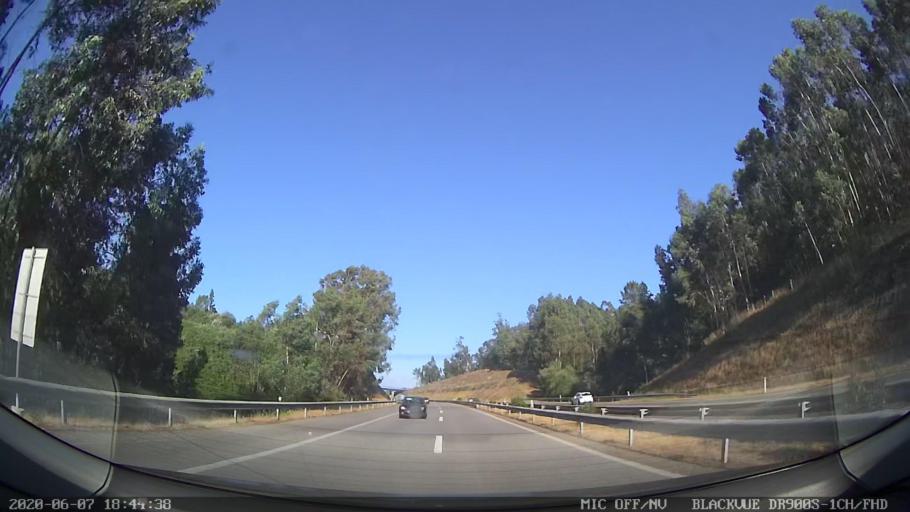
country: PT
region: Braga
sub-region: Vila Nova de Famalicao
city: Joane
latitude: 41.4071
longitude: -8.4197
